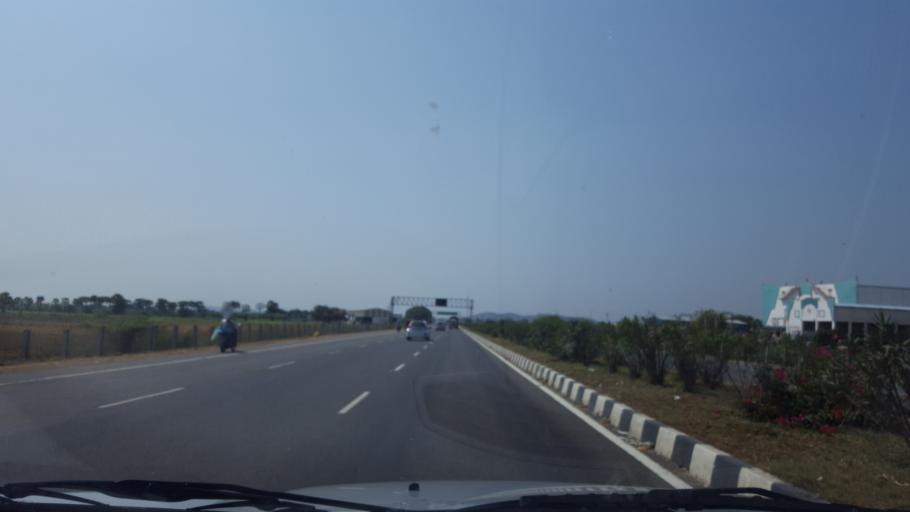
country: IN
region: Andhra Pradesh
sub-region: Guntur
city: Chilakalurupet
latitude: 16.0145
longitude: 80.1197
